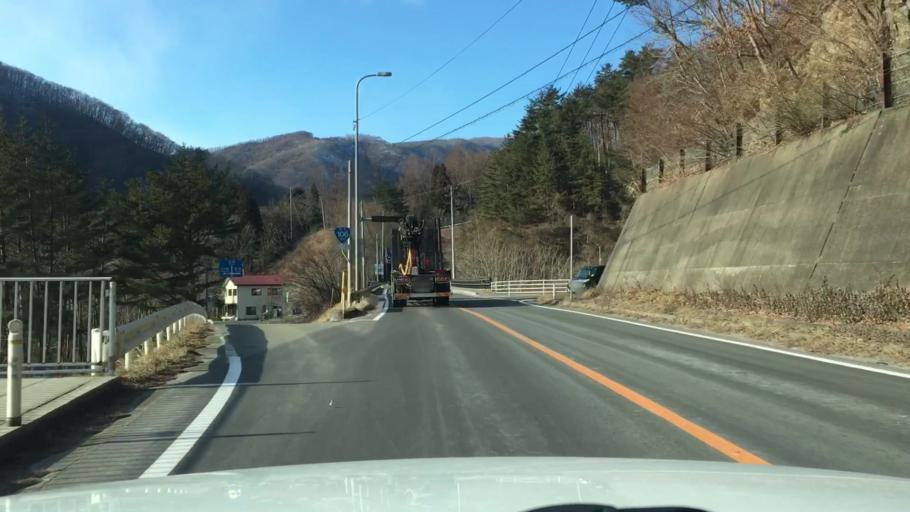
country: JP
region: Iwate
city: Tono
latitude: 39.6416
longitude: 141.5987
